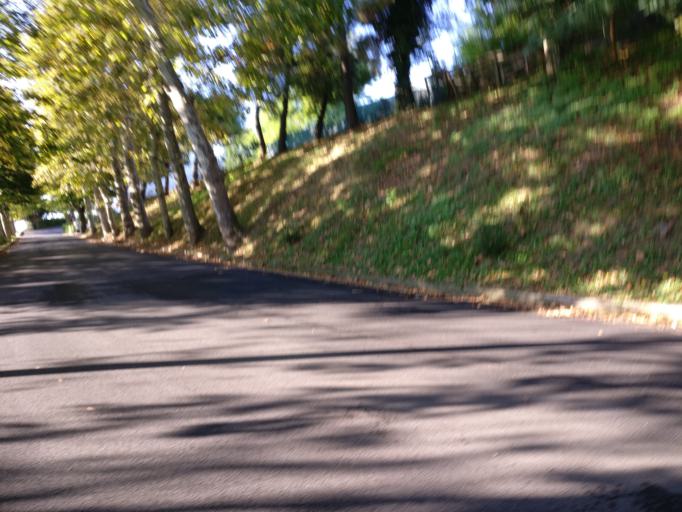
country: IT
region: The Marches
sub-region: Provincia di Ascoli Piceno
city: Montedinove
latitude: 42.9728
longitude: 13.5904
